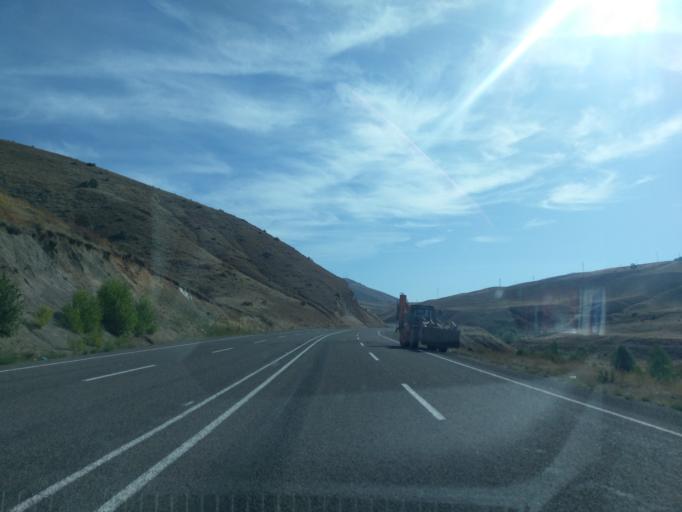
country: TR
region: Sivas
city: Akincilar
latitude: 39.8621
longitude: 38.3384
